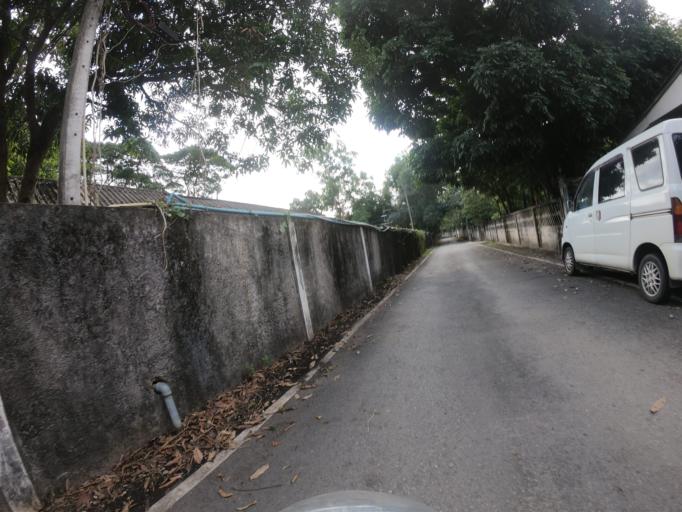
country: TH
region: Chiang Mai
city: Chiang Mai
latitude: 18.8120
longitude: 98.9754
